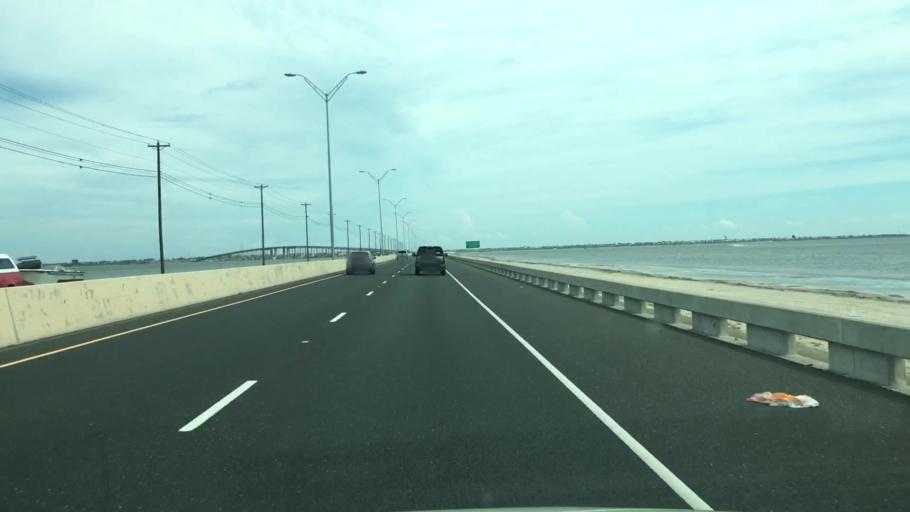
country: US
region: Texas
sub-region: Nueces County
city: Corpus Christi
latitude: 27.6481
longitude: -97.2523
